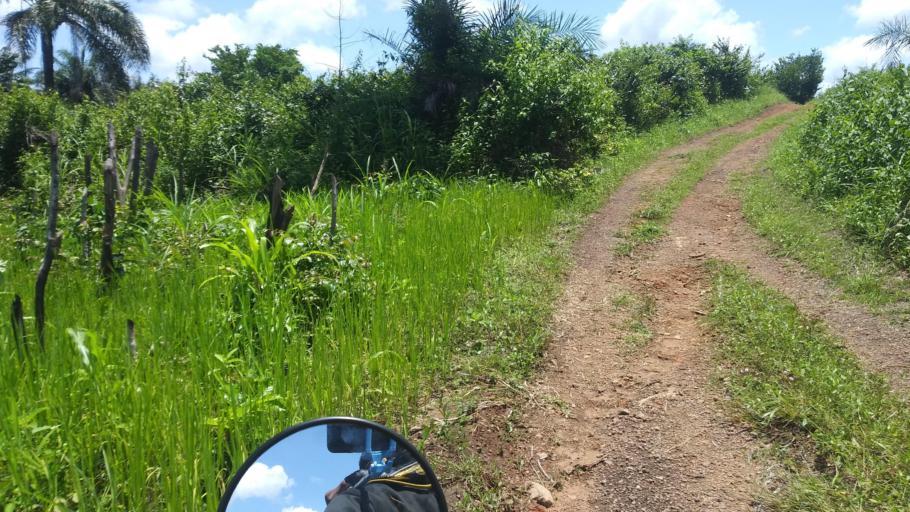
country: SL
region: Northern Province
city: Binkolo
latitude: 8.9107
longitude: -11.9780
